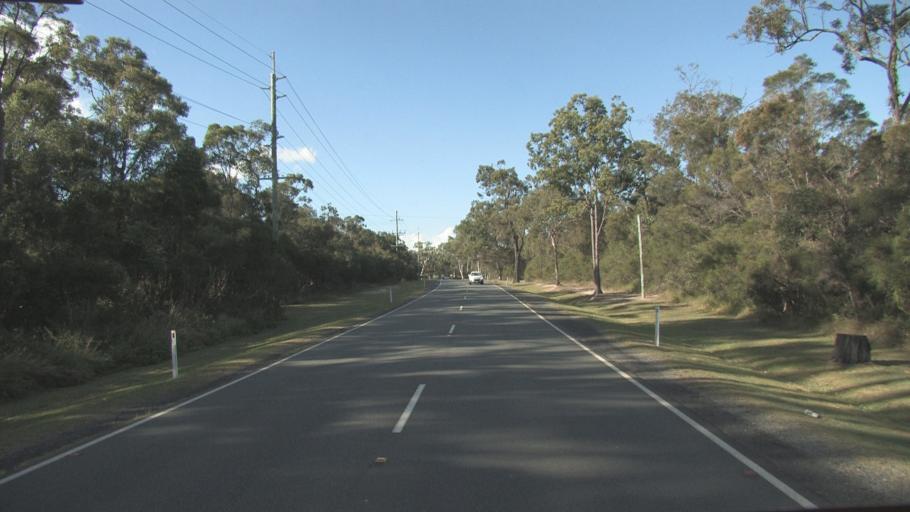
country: AU
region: Queensland
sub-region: Logan
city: Beenleigh
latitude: -27.6595
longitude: 153.2192
